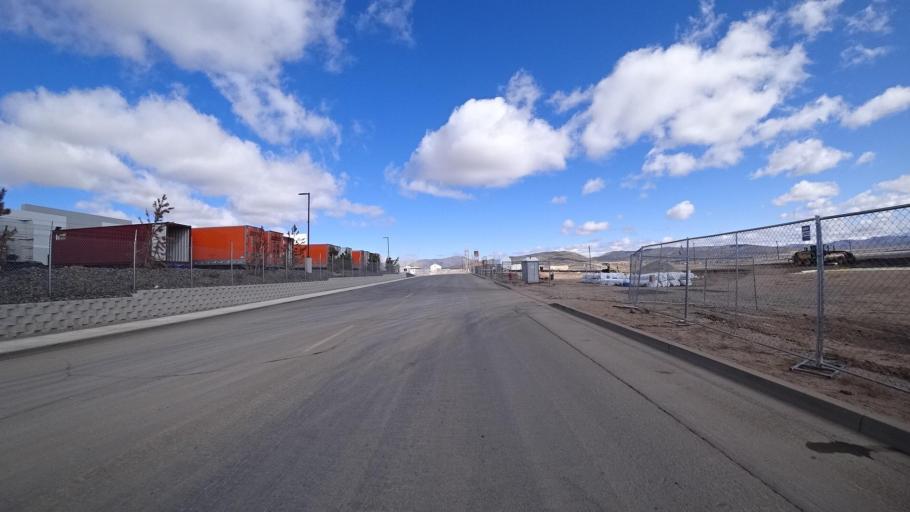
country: US
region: Nevada
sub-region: Washoe County
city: Lemmon Valley
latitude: 39.6542
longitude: -119.8696
